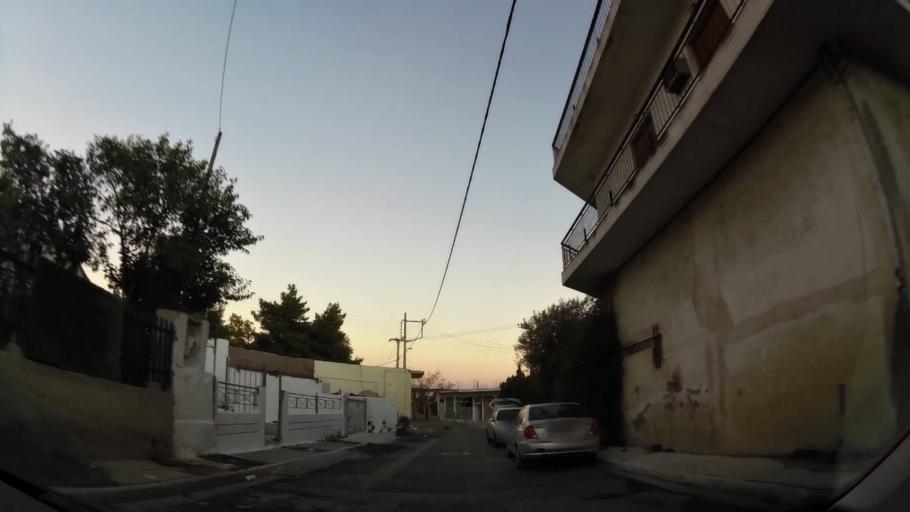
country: GR
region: Attica
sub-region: Nomarchia Dytikis Attikis
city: Ano Liosia
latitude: 38.0807
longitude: 23.6960
